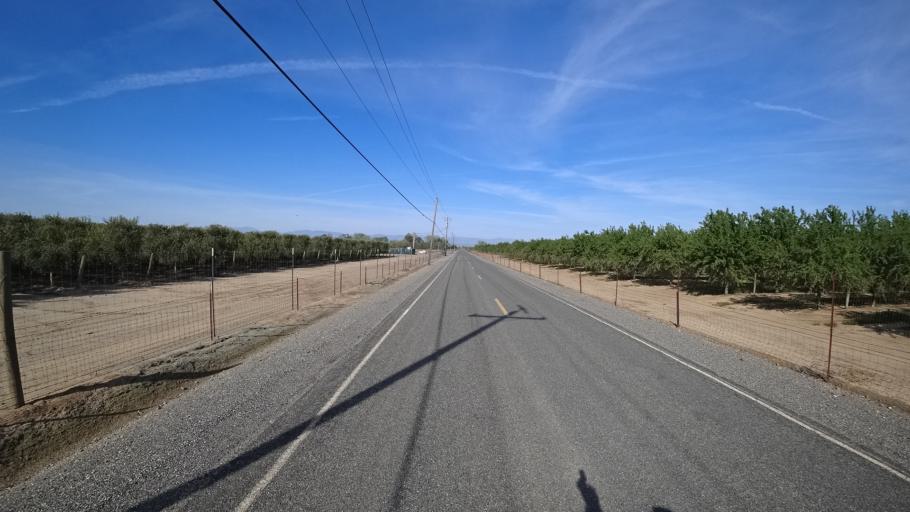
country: US
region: California
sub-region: Glenn County
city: Orland
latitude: 39.6679
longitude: -122.2107
